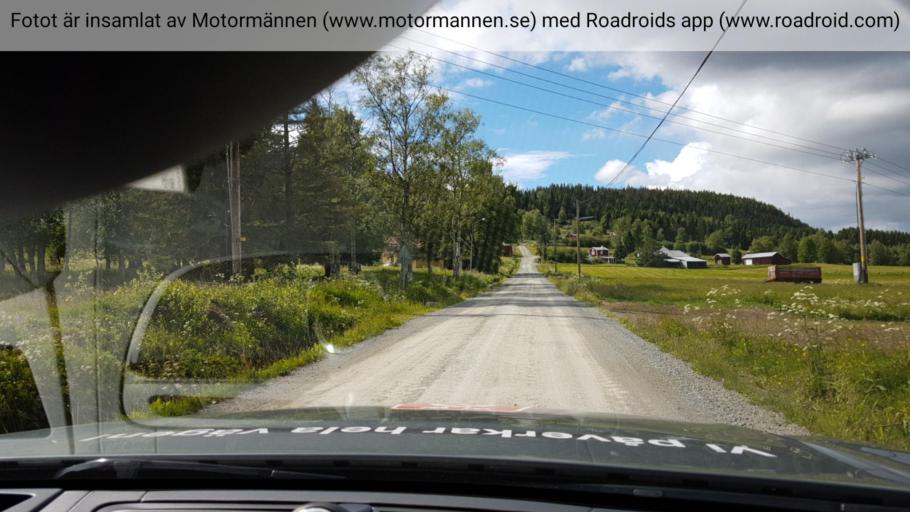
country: SE
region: Jaemtland
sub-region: Bergs Kommun
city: Hoverberg
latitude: 62.9179
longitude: 14.3112
